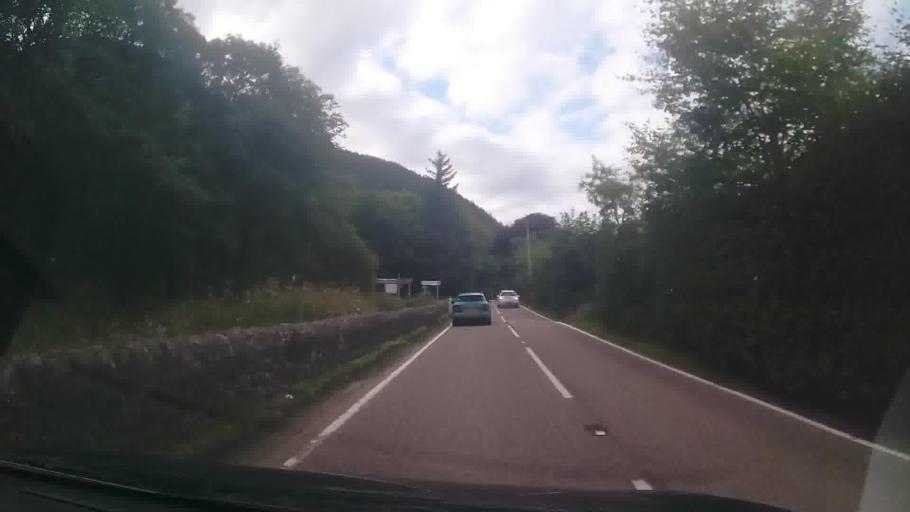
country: GB
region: Scotland
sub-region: Highland
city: Fort William
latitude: 56.6859
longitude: -5.1938
